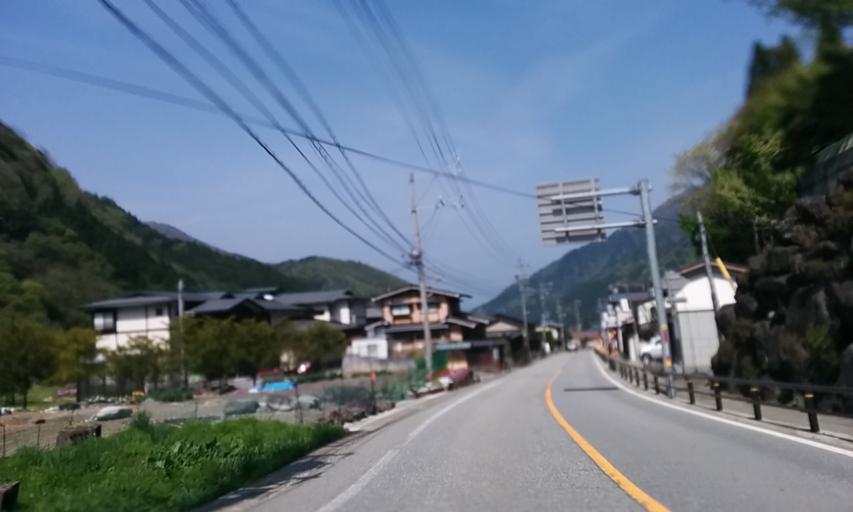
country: JP
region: Gifu
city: Takayama
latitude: 36.2428
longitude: 137.5203
